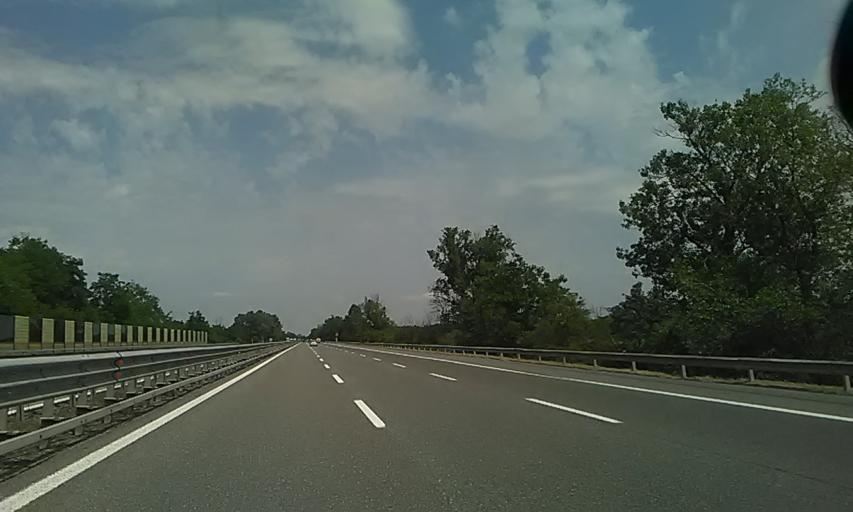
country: IT
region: Piedmont
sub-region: Provincia di Alessandria
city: Silvano d'Orba
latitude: 44.6939
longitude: 8.6659
